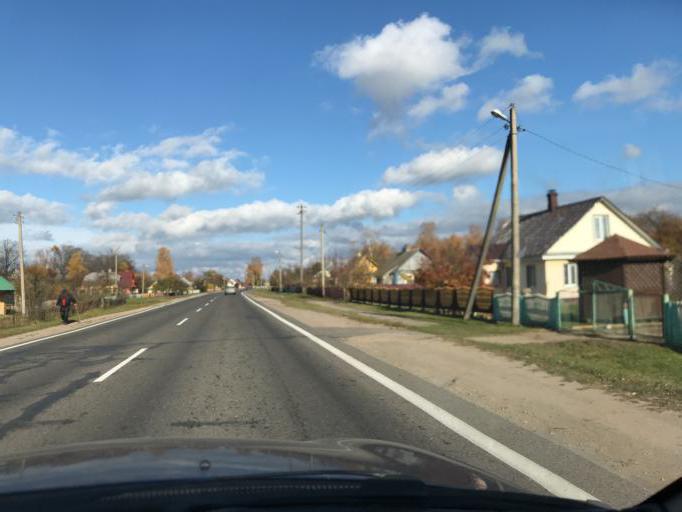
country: LT
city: Salcininkai
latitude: 54.2388
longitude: 25.3551
